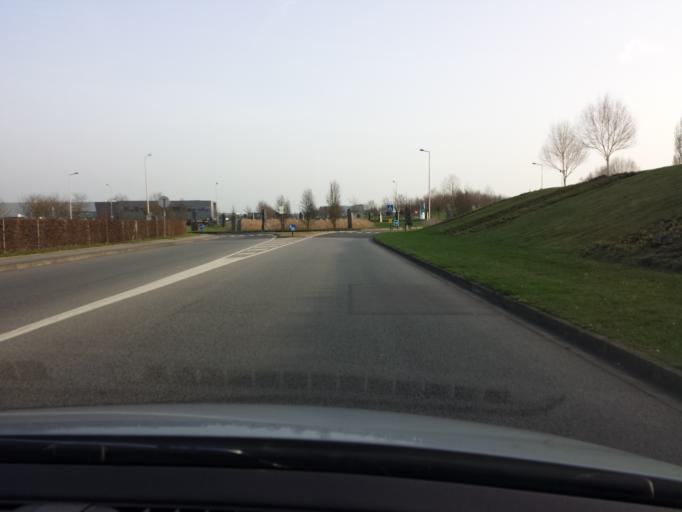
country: FR
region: Haute-Normandie
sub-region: Departement de l'Eure
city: Evreux
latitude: 49.0067
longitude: 1.1703
